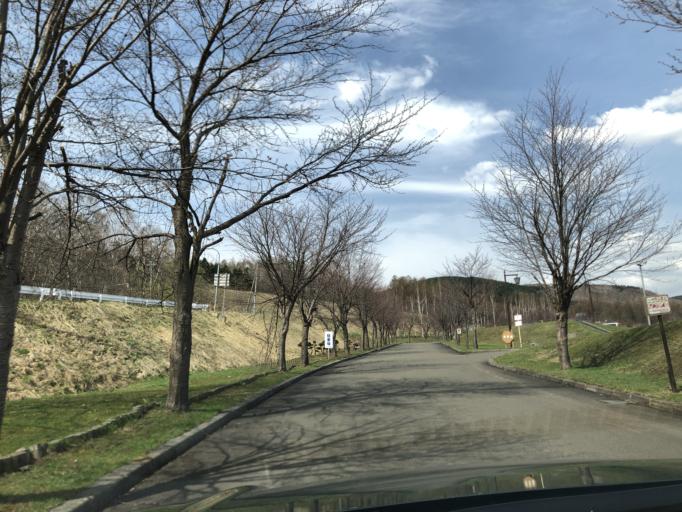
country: JP
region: Hokkaido
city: Akabira
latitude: 43.5942
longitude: 142.0453
